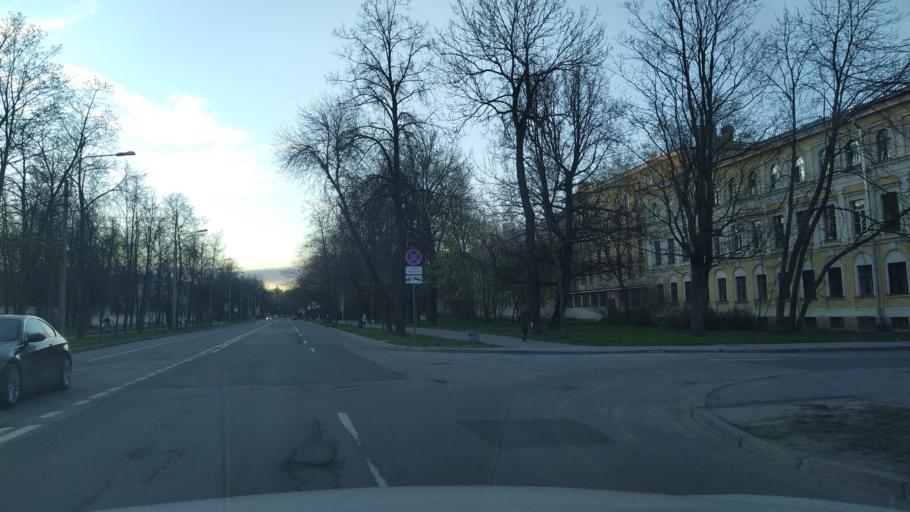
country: RU
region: St.-Petersburg
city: Pushkin
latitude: 59.7059
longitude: 30.4055
